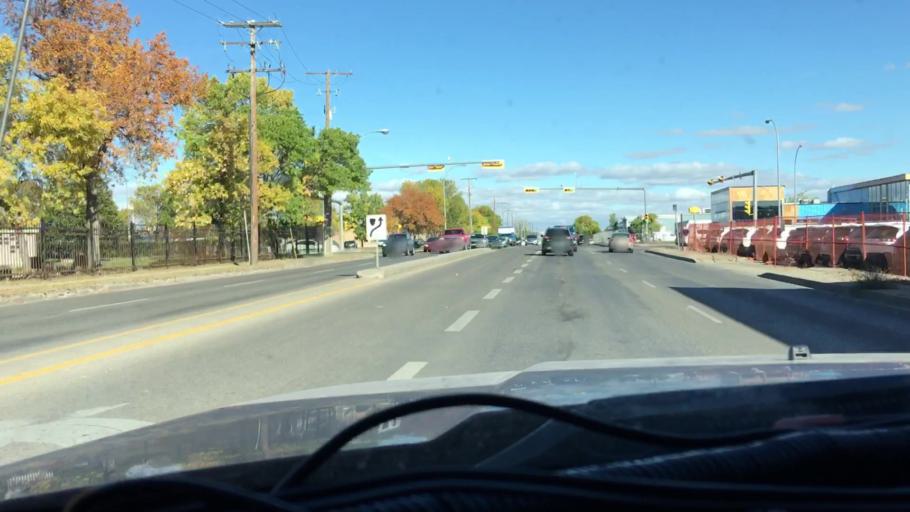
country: CA
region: Saskatchewan
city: Regina
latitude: 50.4629
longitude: -104.6076
